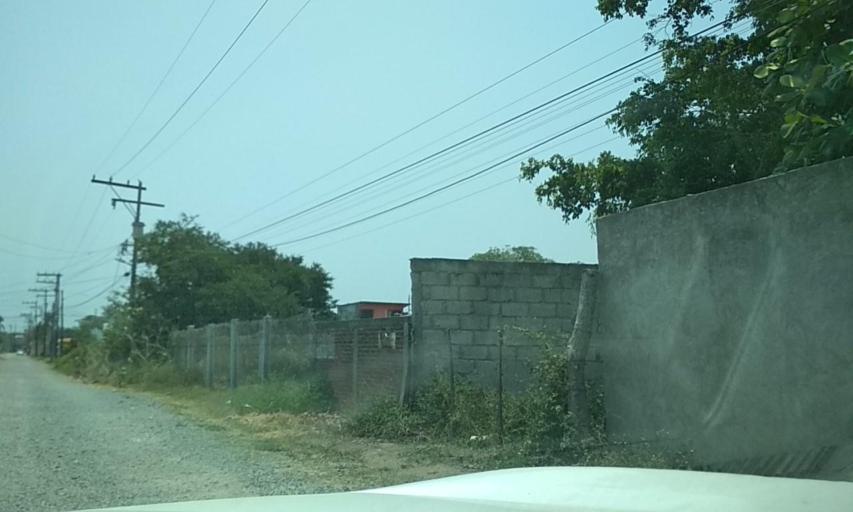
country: MX
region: Veracruz
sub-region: Veracruz
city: Las Amapolas
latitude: 19.1586
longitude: -96.1871
